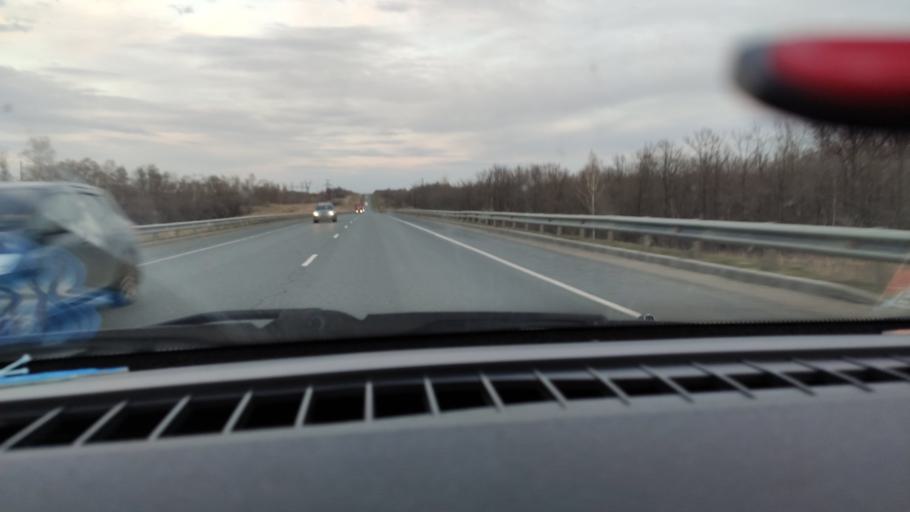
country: RU
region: Saratov
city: Yelshanka
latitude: 51.8221
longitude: 46.3282
